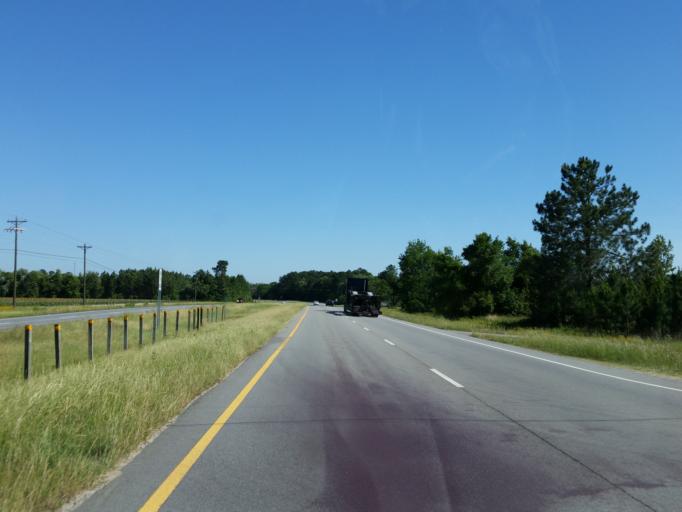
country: US
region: Georgia
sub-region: Lowndes County
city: Valdosta
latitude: 30.7729
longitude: -83.2307
